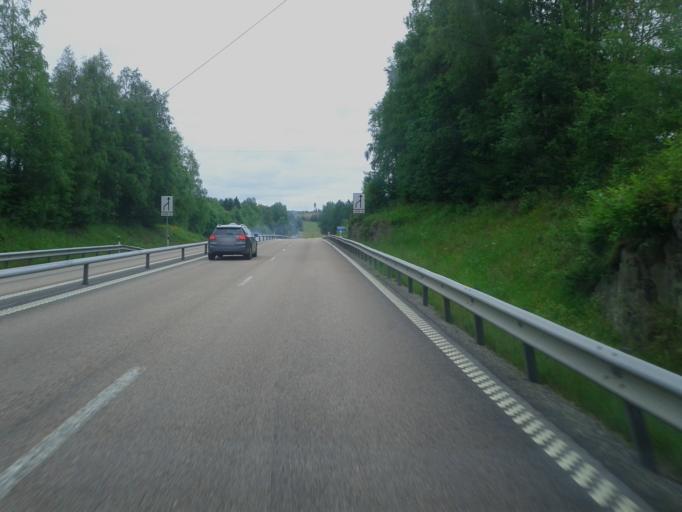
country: SE
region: Vaesternorrland
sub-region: OErnskoeldsviks Kommun
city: Bjasta
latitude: 63.1613
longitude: 18.4204
